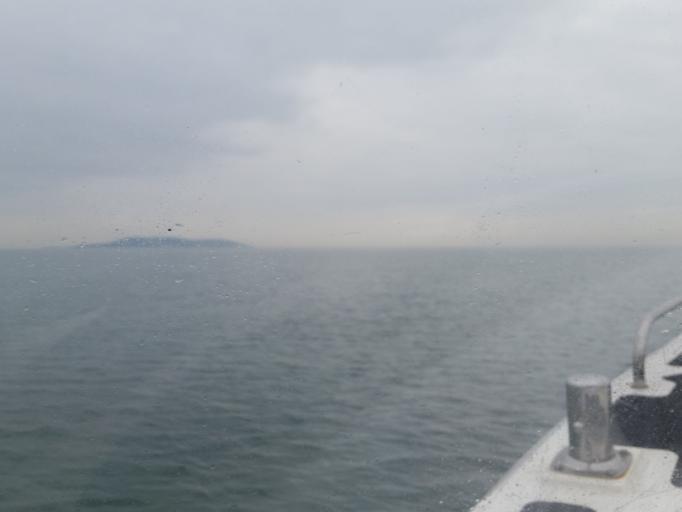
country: IE
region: Leinster
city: Malahide
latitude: 53.4508
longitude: -6.1236
